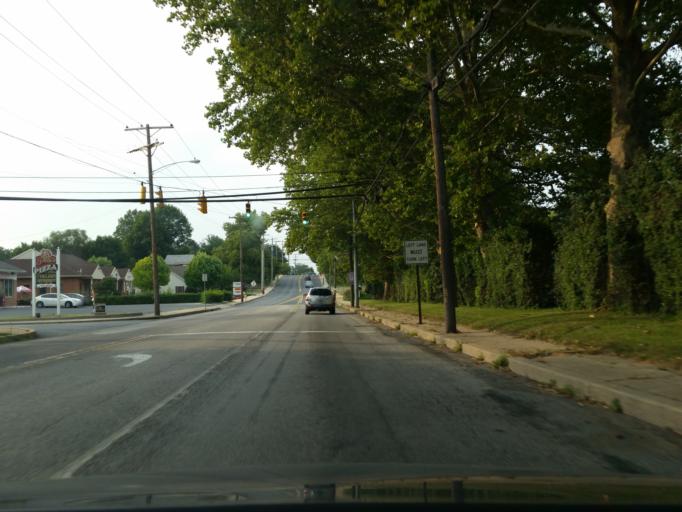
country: US
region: Pennsylvania
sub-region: Lebanon County
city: Lebanon South
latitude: 40.3218
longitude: -76.4248
